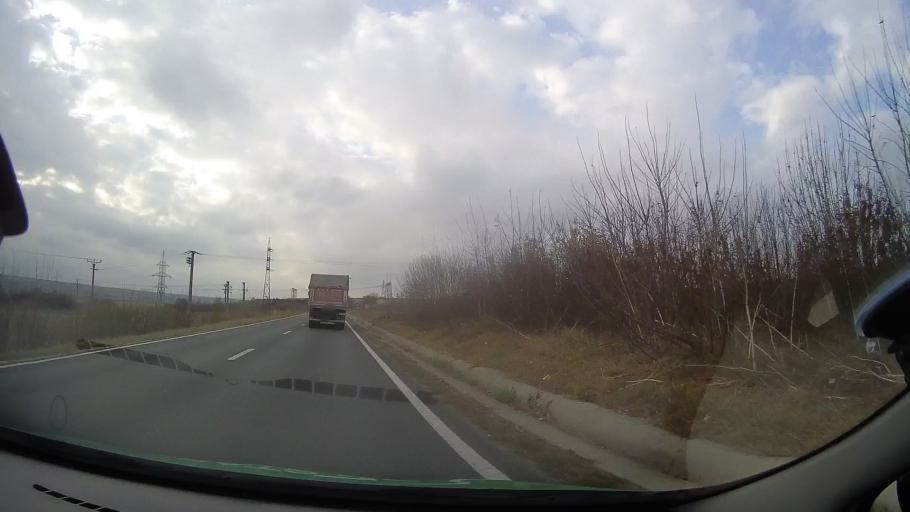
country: RO
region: Constanta
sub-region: Comuna Mircea Voda
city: Satu Nou
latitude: 44.2708
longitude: 28.2019
